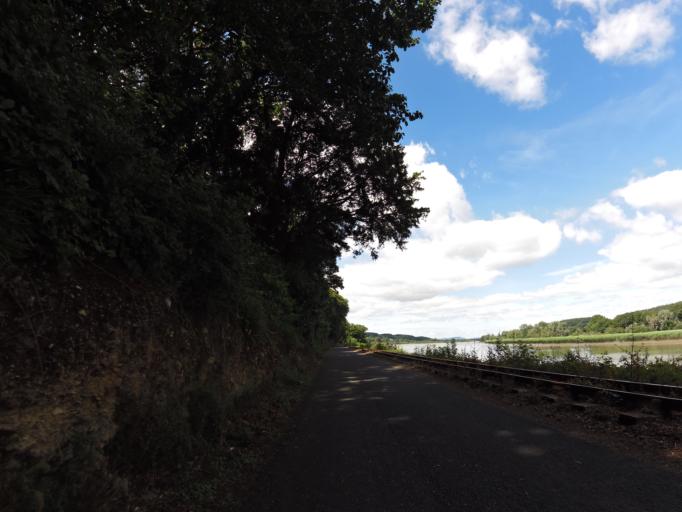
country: IE
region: Leinster
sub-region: Kilkenny
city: Mooncoin
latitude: 52.2431
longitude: -7.2228
